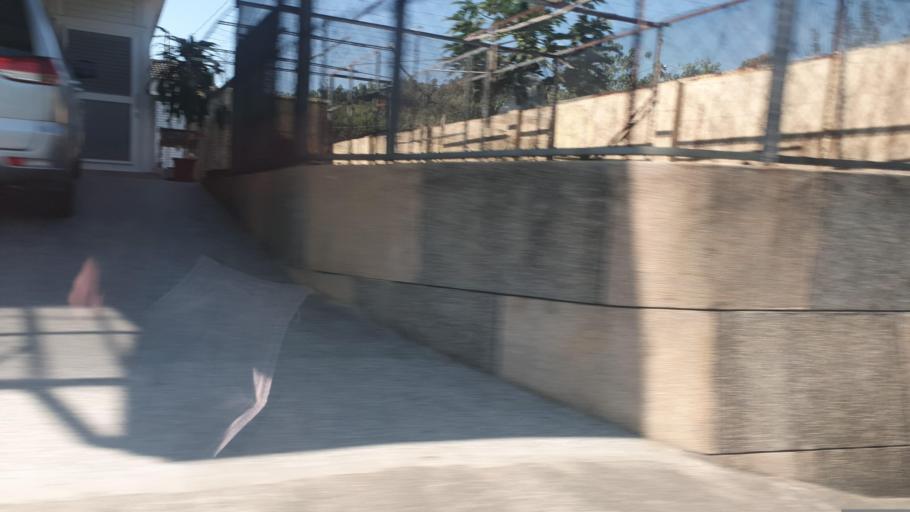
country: TW
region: Taiwan
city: Yujing
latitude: 23.0635
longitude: 120.3814
